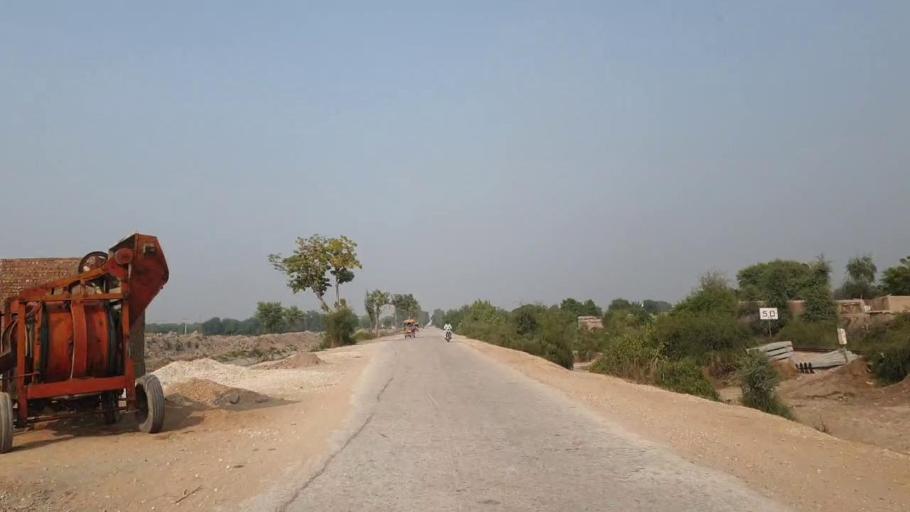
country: PK
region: Sindh
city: Bhan
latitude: 26.5814
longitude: 67.7286
